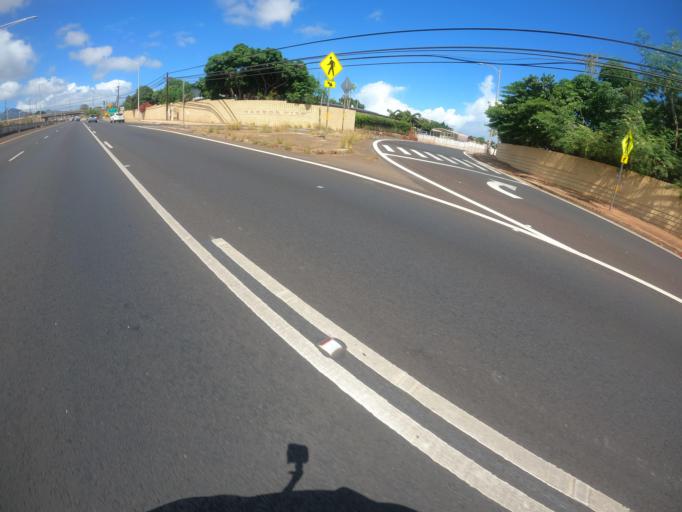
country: US
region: Hawaii
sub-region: Honolulu County
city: Royal Kunia
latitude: 21.3812
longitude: -158.0300
